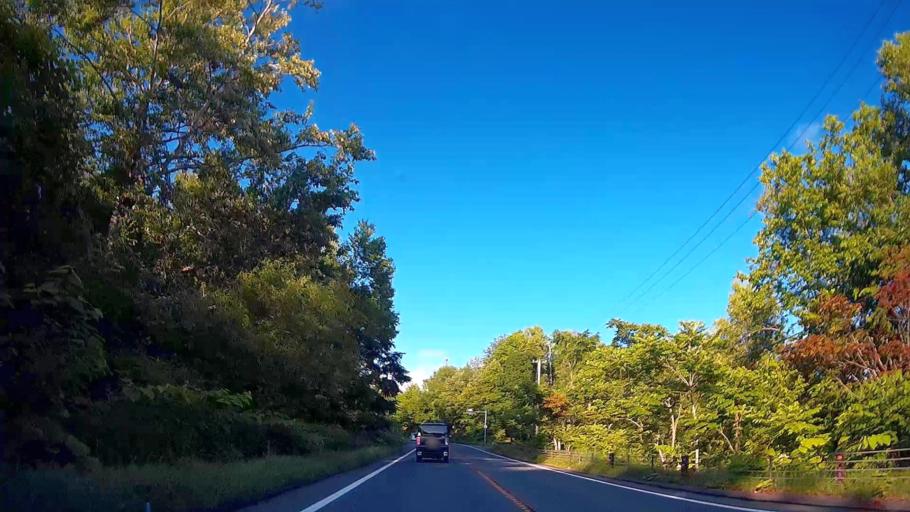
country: JP
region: Hokkaido
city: Date
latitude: 42.6128
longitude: 140.7828
